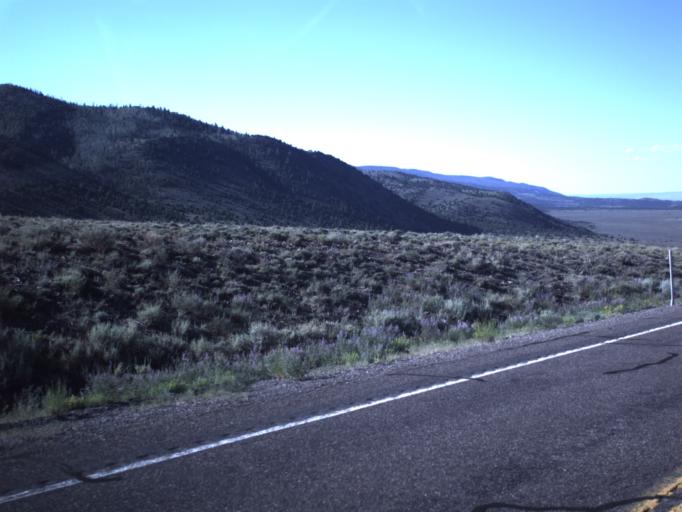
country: US
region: Utah
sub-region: Wayne County
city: Loa
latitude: 38.5426
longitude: -111.5116
